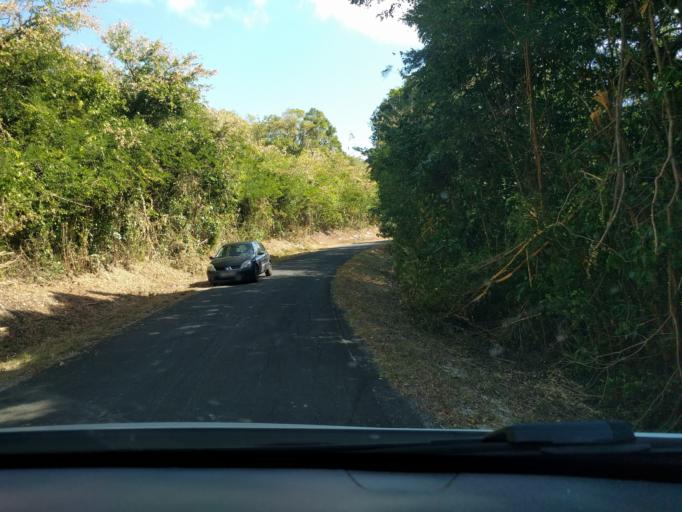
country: GP
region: Guadeloupe
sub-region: Guadeloupe
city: Grand-Bourg
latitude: 15.9737
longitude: -61.2594
